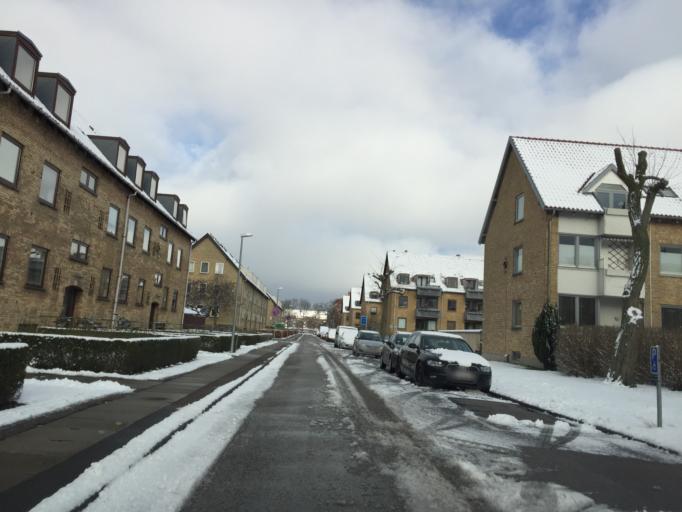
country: DK
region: Capital Region
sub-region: Tarnby Kommune
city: Tarnby
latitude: 55.6321
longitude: 12.6430
